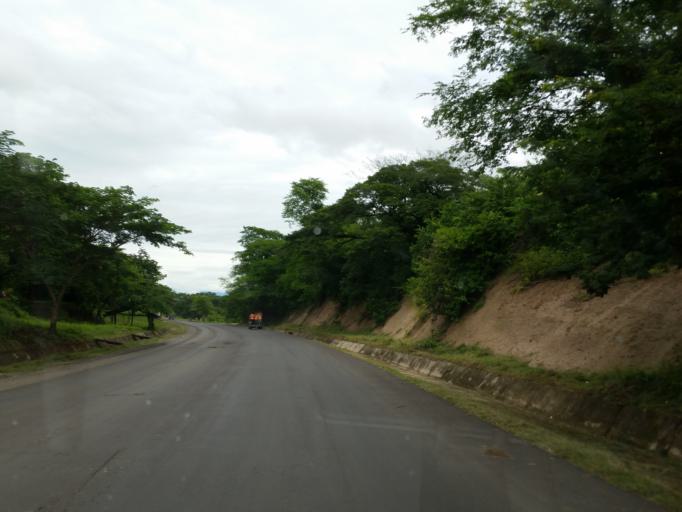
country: NI
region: Chinandega
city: Somotillo
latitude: 12.8656
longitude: -86.8512
